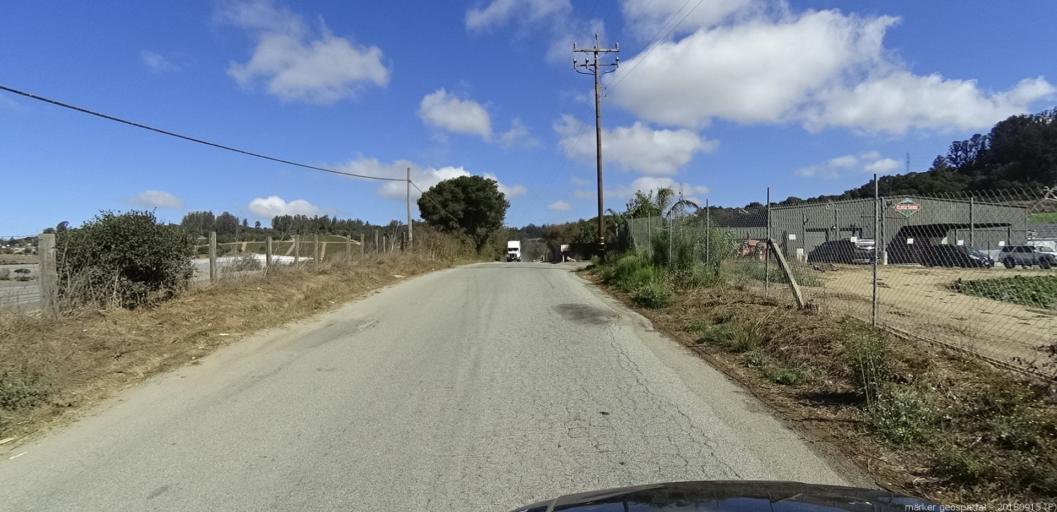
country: US
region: California
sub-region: Monterey County
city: Las Lomas
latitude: 36.8667
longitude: -121.7226
